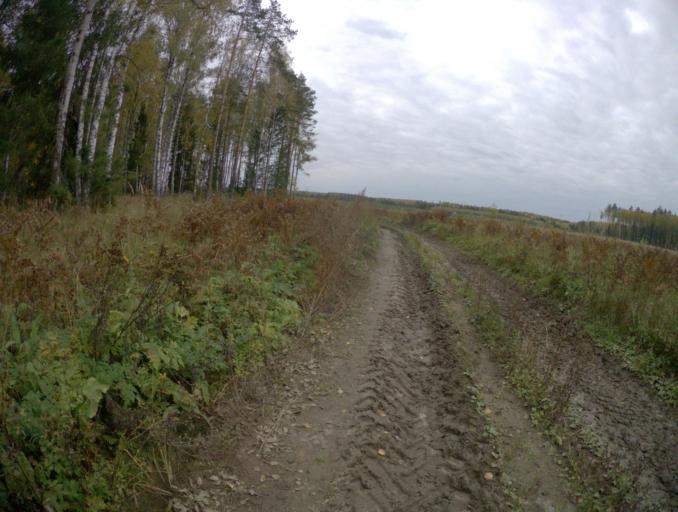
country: RU
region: Vladimir
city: Stepantsevo
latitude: 56.3152
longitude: 41.5567
